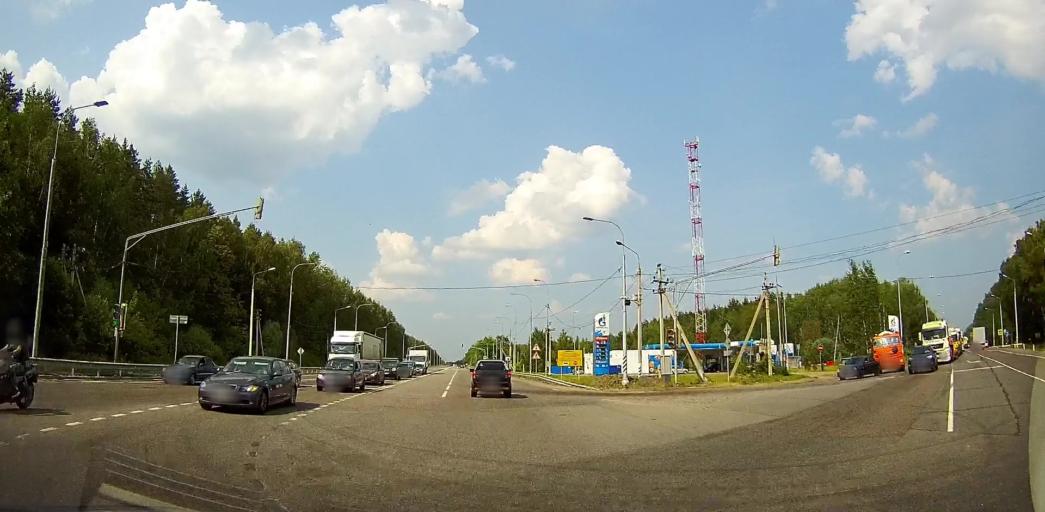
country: RU
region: Moskovskaya
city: Mikhnevo
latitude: 55.0773
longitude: 37.9521
